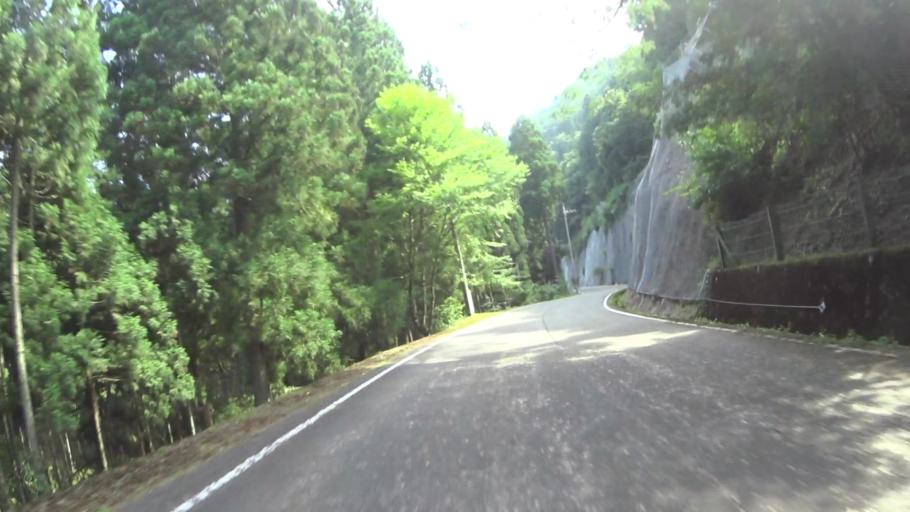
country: JP
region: Fukui
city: Obama
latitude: 35.3112
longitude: 135.6421
